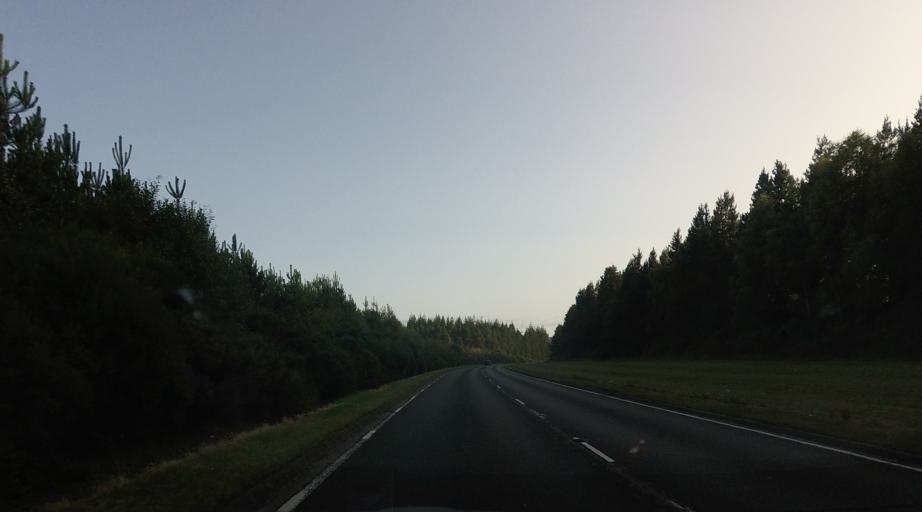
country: GB
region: Scotland
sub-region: Highland
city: Dingwall
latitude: 57.5569
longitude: -4.3343
